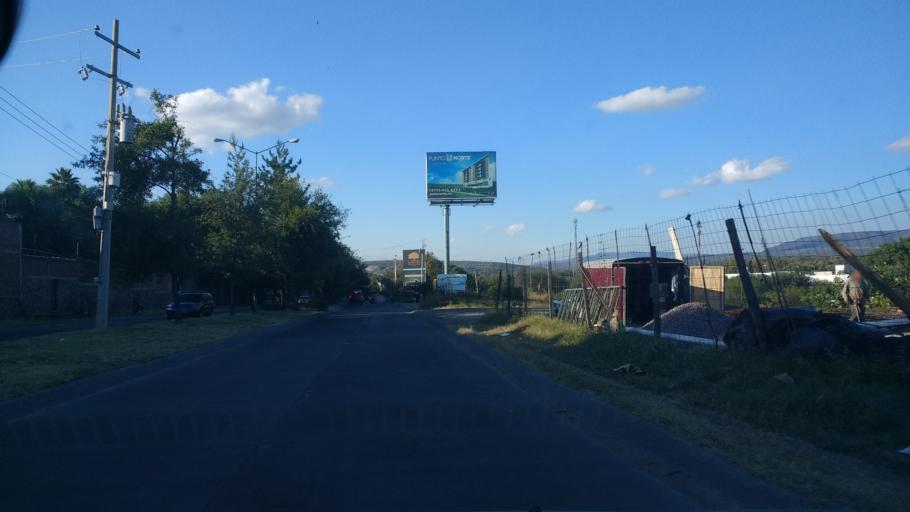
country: MX
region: Guanajuato
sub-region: Leon
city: La Ermita
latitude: 21.1795
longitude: -101.7038
